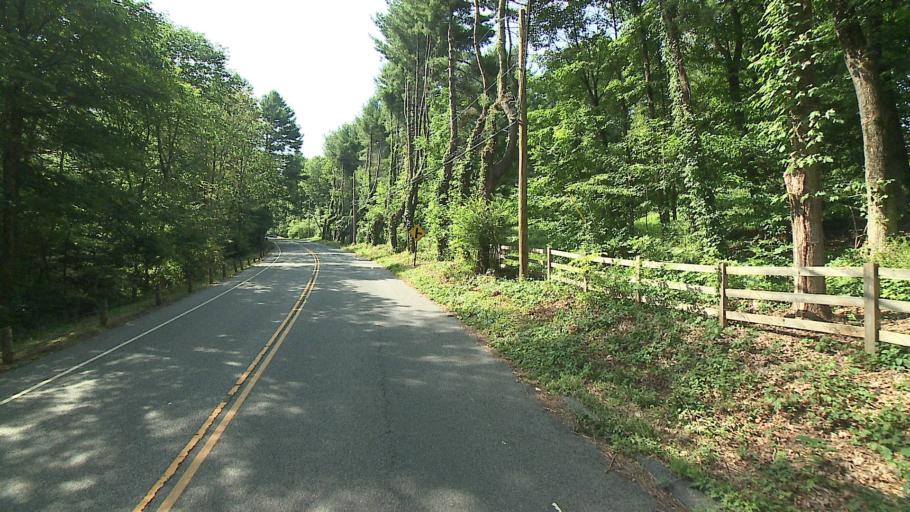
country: US
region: Connecticut
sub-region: Fairfield County
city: Sherman
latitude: 41.5652
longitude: -73.5071
